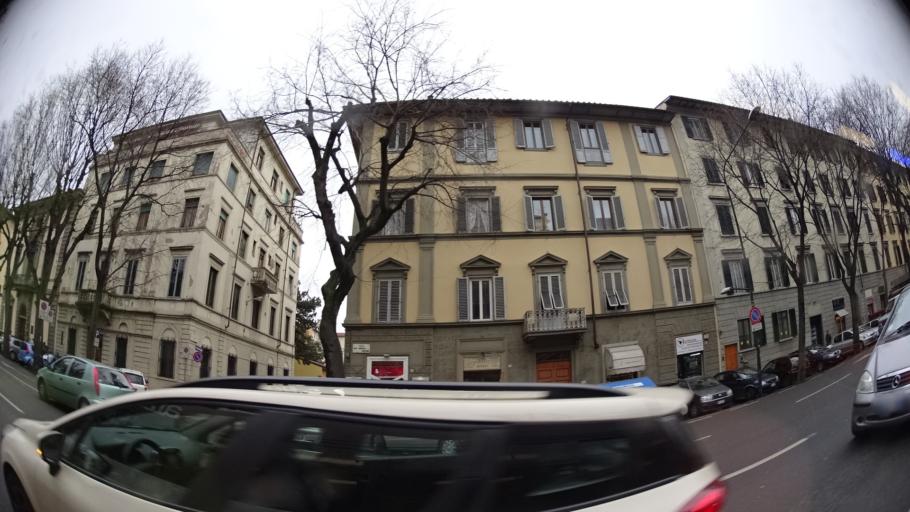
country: IT
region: Tuscany
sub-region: Province of Florence
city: Florence
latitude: 43.7867
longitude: 11.2681
